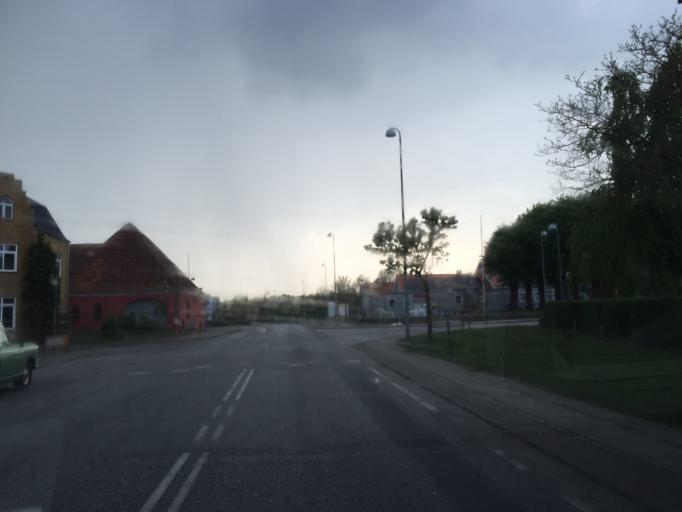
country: DK
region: South Denmark
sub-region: Sonderborg Kommune
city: Grasten
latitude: 54.9957
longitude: 9.5836
